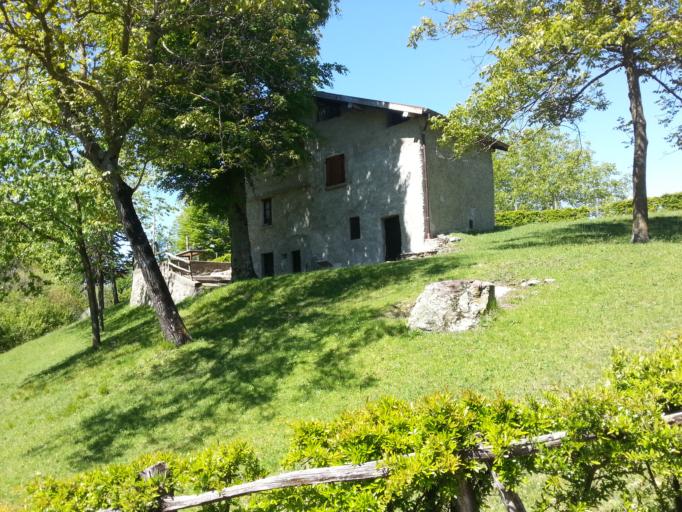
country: IT
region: Lombardy
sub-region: Provincia di Como
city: Plesio
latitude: 46.0435
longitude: 9.2190
